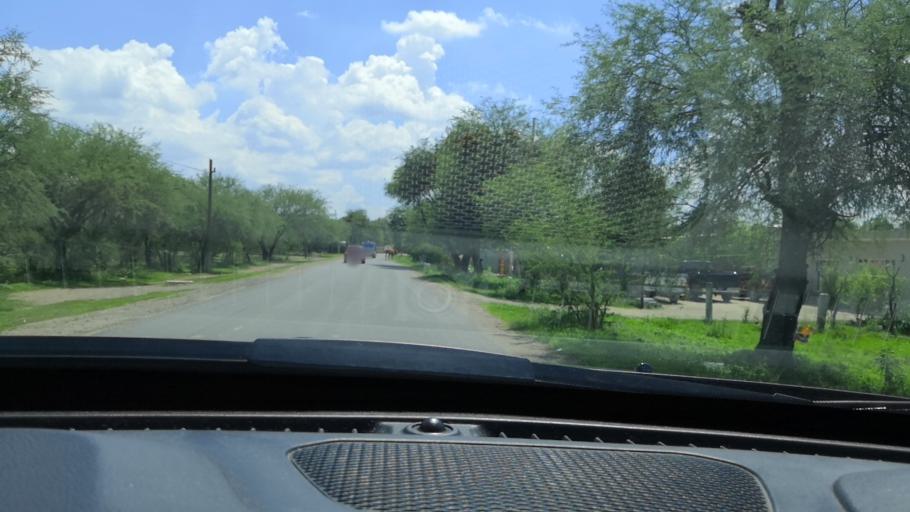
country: MX
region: Guanajuato
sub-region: Leon
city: Plan Guanajuato (La Sandia)
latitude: 20.9378
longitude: -101.6371
